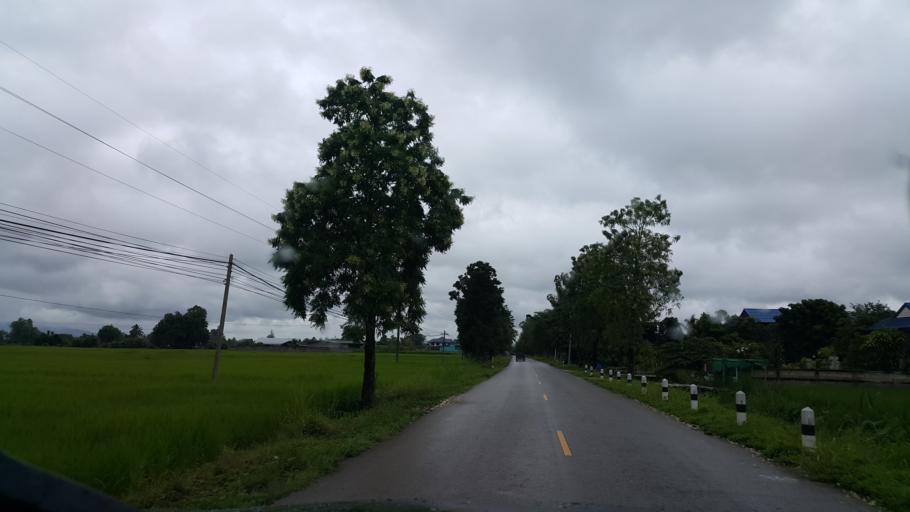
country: TH
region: Phayao
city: Chiang Kham
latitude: 19.5232
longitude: 100.3575
